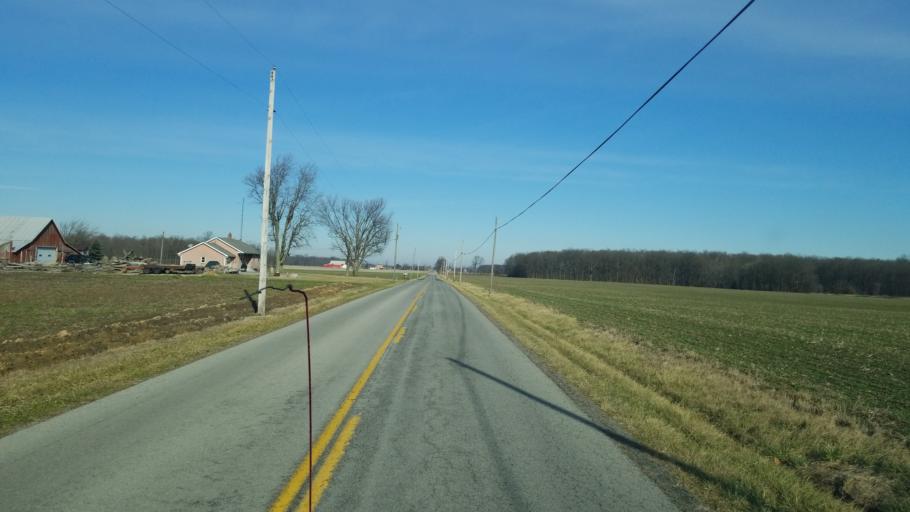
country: US
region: Ohio
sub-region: Allen County
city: Bluffton
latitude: 40.8484
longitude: -83.8994
